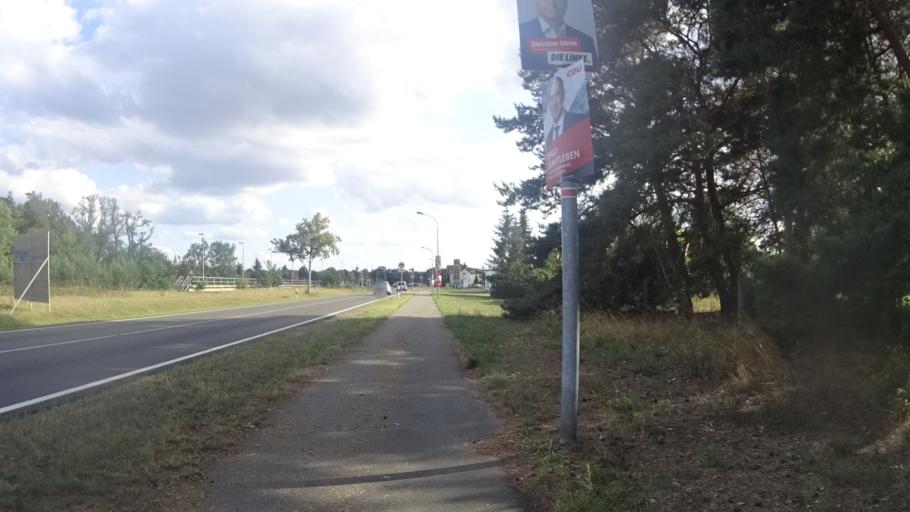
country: DE
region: Brandenburg
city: Premnitz
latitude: 52.5614
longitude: 12.3298
